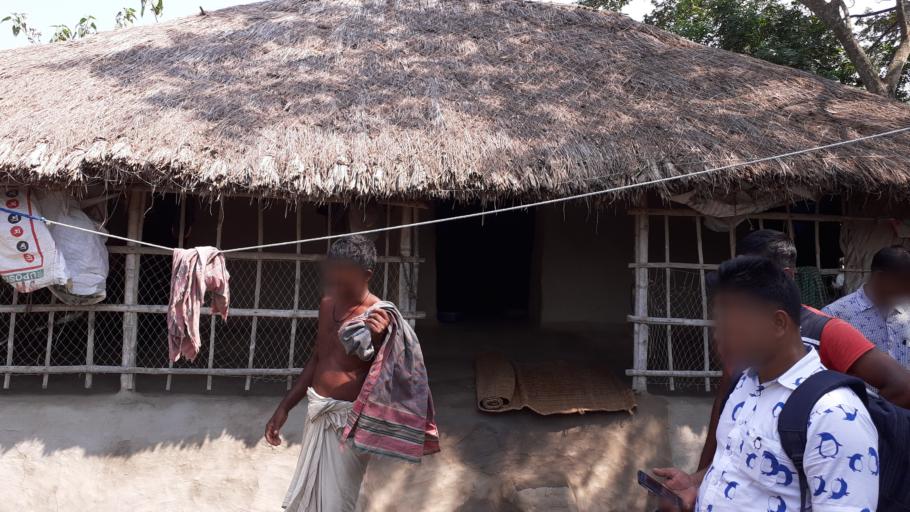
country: BD
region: Khulna
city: Phultala
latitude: 22.6450
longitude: 89.4004
